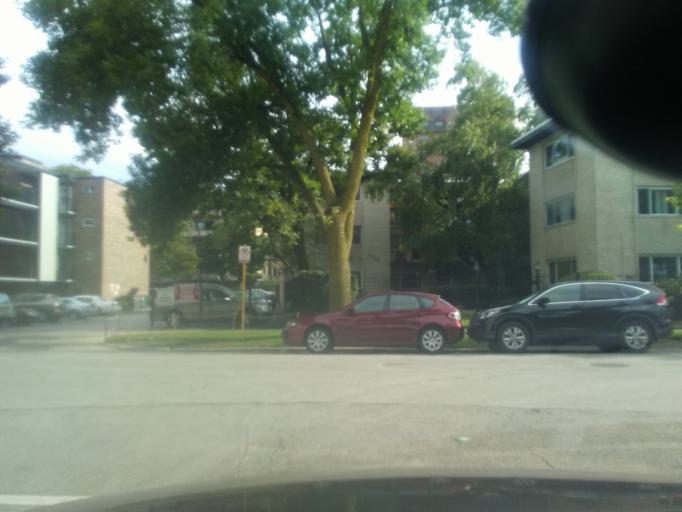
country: US
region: Illinois
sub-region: Cook County
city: Evanston
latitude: 42.0184
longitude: -87.6643
